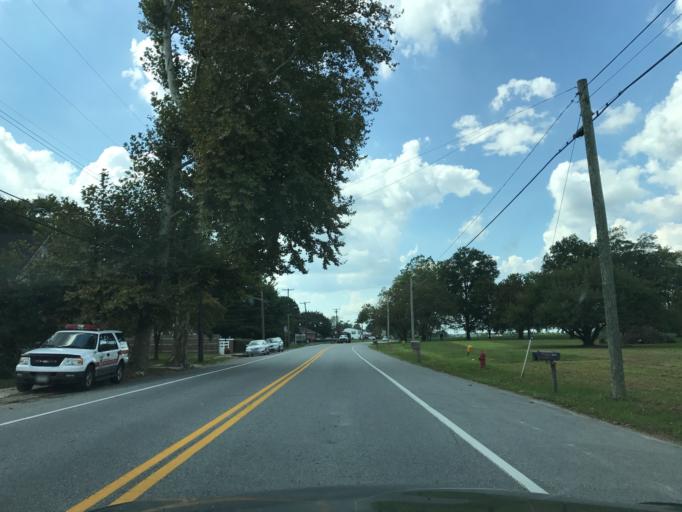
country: US
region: Maryland
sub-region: Queen Anne's County
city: Kingstown
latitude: 39.1868
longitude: -75.8600
